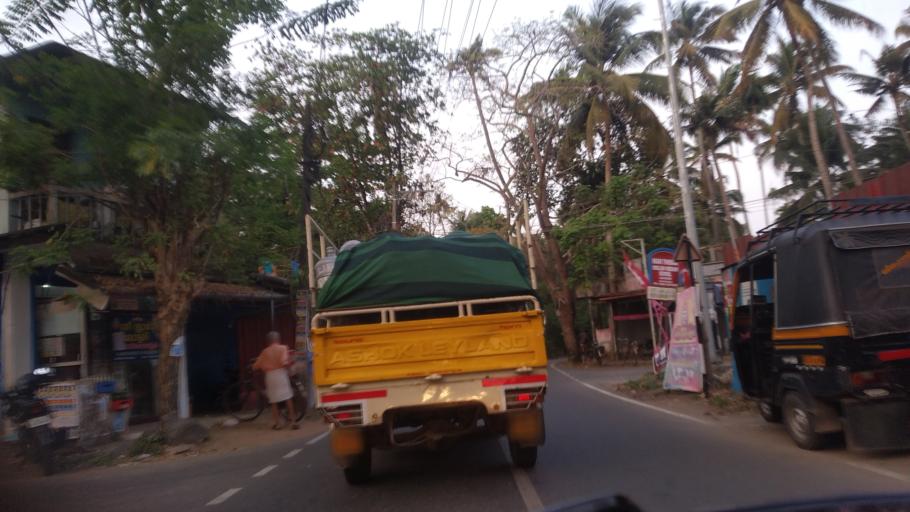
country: IN
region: Kerala
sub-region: Thrissur District
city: Kodungallur
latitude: 10.1998
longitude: 76.1752
